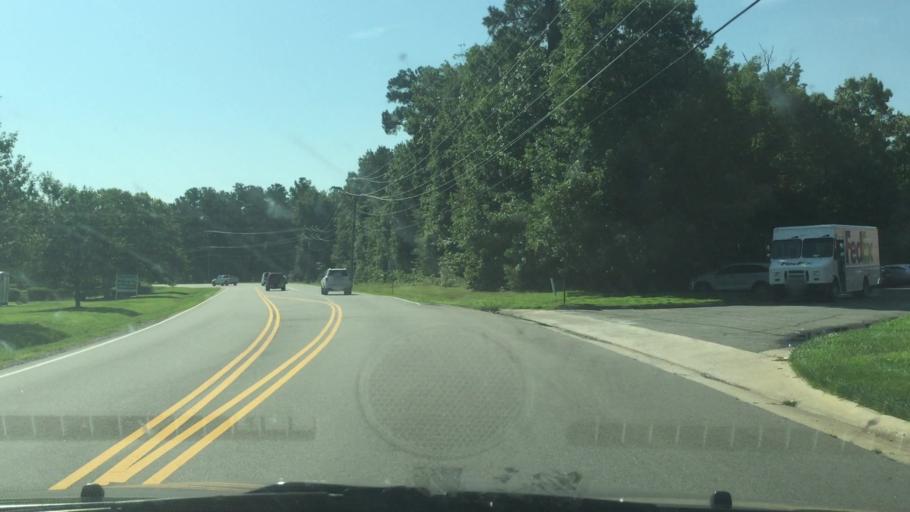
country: US
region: Virginia
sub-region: Hanover County
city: Ashland
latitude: 37.7441
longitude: -77.4685
